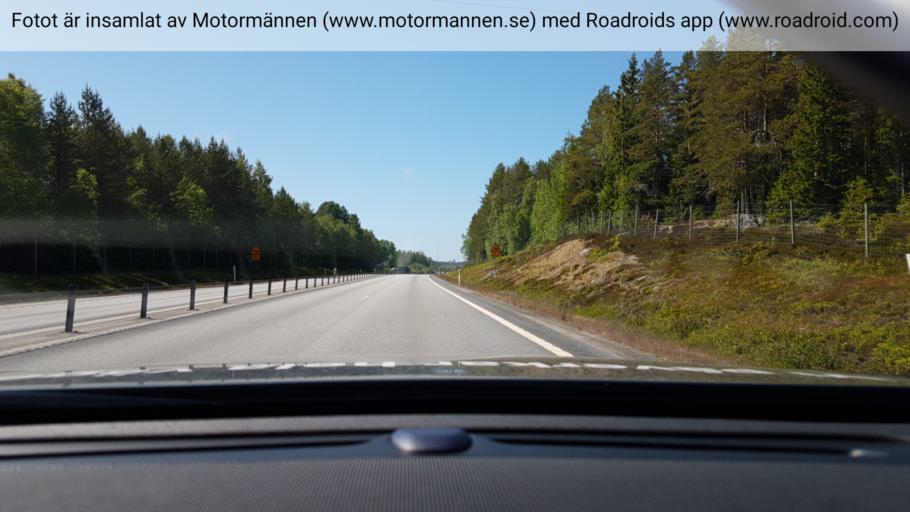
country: SE
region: Vaesterbotten
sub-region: Umea Kommun
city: Roback
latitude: 63.7526
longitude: 20.1531
